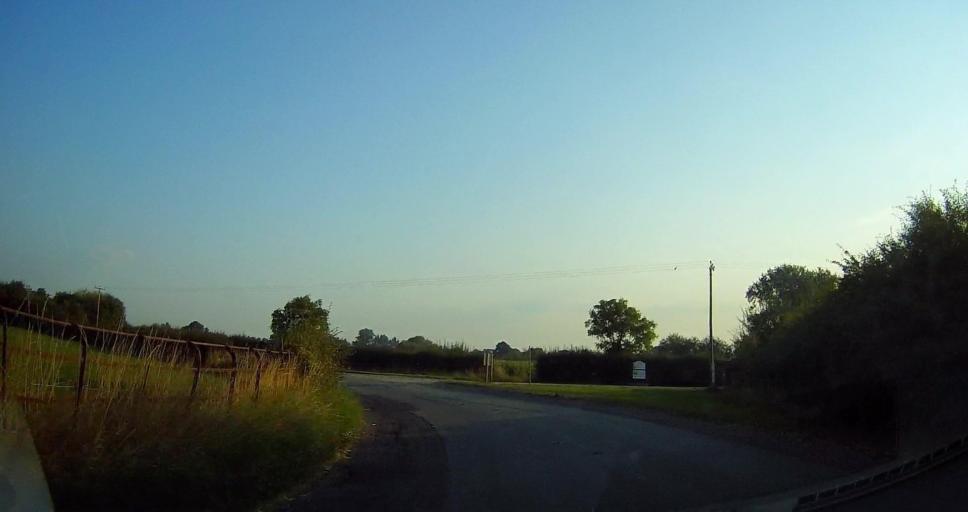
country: GB
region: England
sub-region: Cheshire East
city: Nantwich
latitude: 53.0477
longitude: -2.5196
